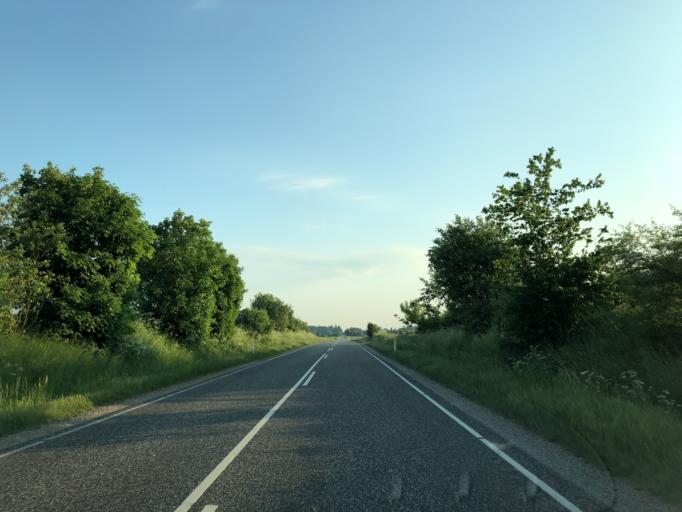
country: DK
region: Central Jutland
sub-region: Struer Kommune
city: Struer
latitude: 56.4401
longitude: 8.5287
